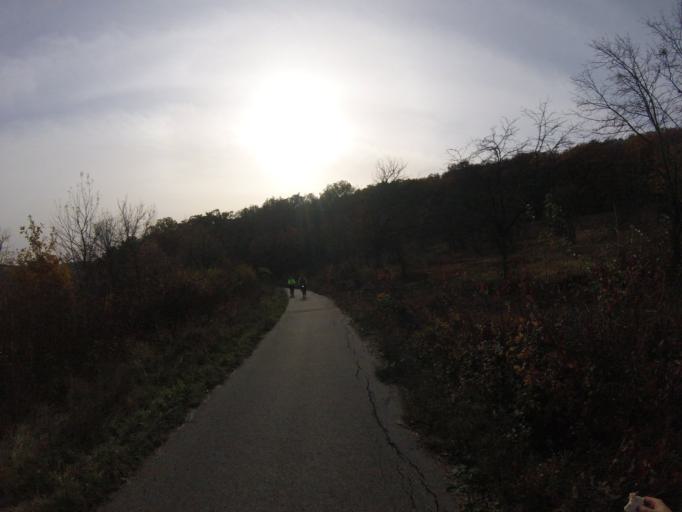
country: HU
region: Borsod-Abauj-Zemplen
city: Gonc
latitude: 48.5201
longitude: 21.4568
